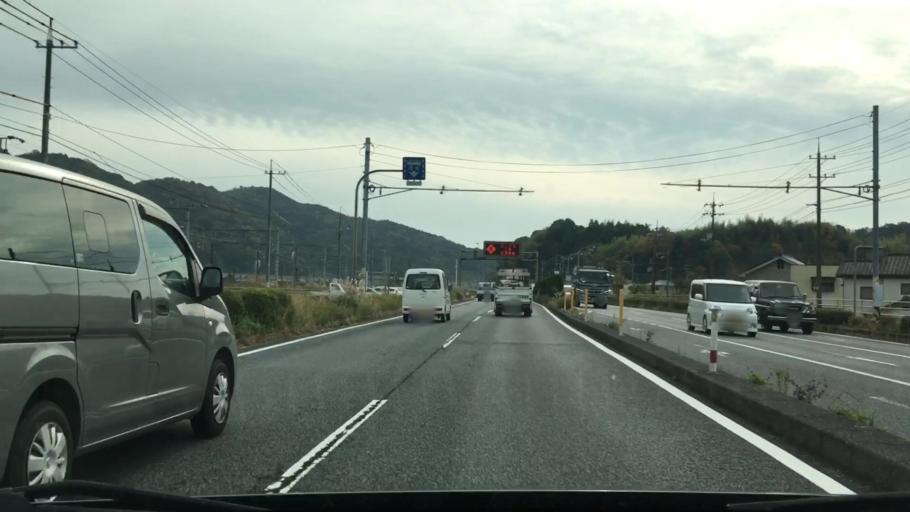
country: JP
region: Yamaguchi
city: Tokuyama
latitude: 34.0760
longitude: 131.7060
